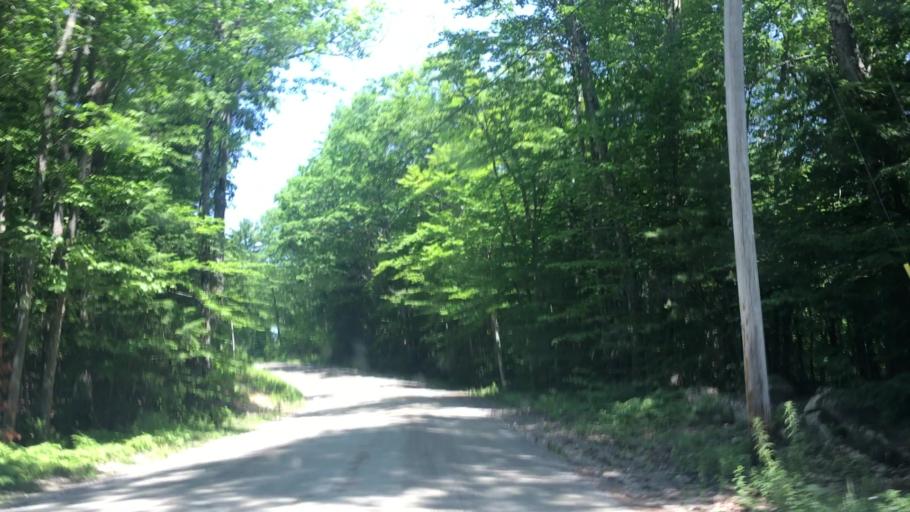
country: US
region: Maine
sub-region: Kennebec County
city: Wayne
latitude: 44.3089
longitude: -70.0543
